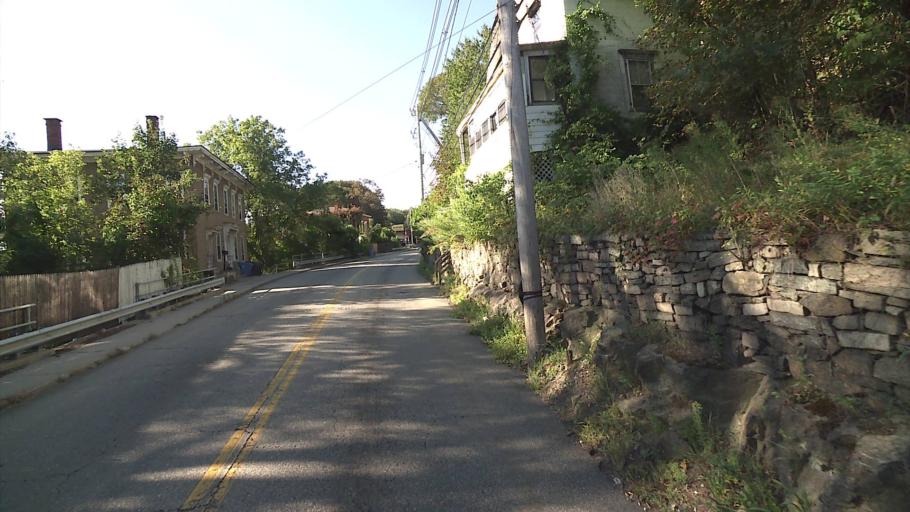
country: US
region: Connecticut
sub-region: New London County
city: Norwich
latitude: 41.5173
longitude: -72.0800
